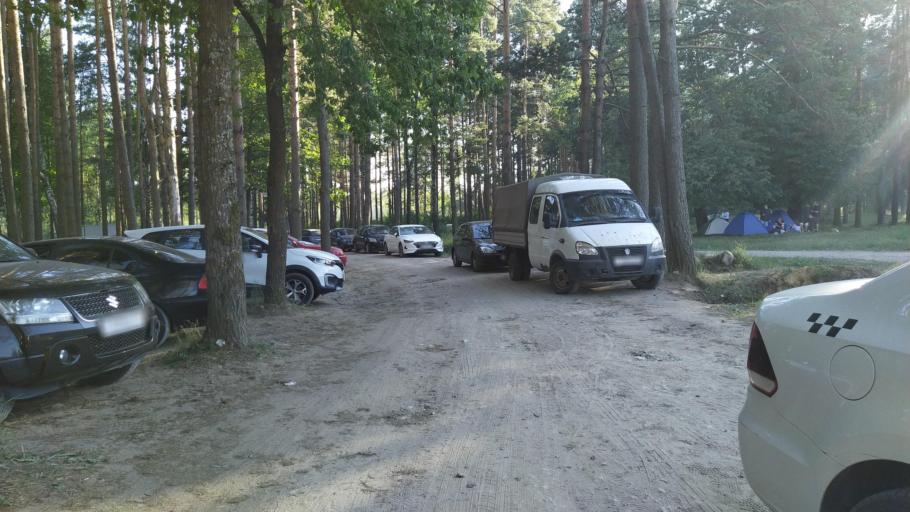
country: RU
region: Leningrad
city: Koltushi
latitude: 59.9191
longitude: 30.7362
